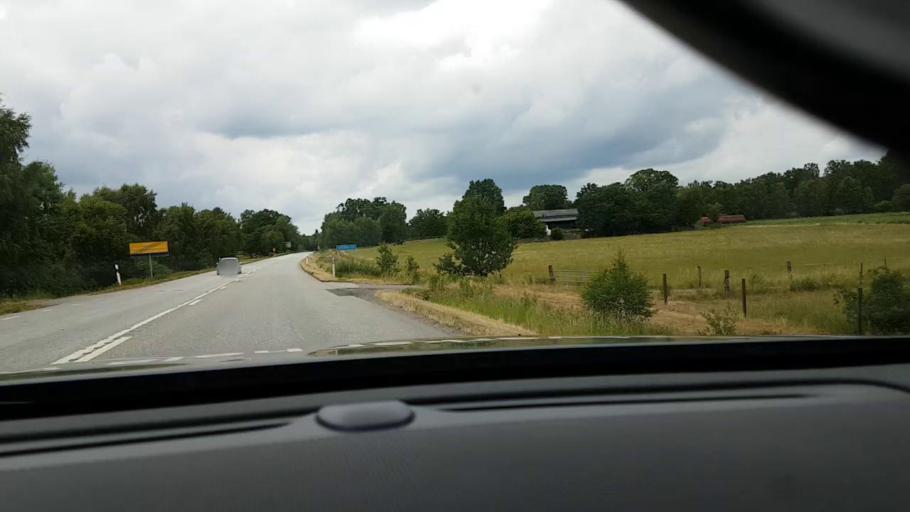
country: SE
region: Skane
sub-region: Horby Kommun
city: Hoerby
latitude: 55.8613
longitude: 13.6394
